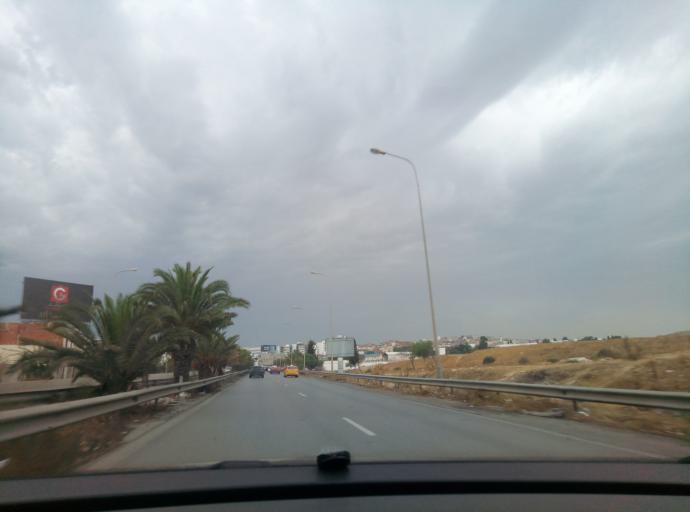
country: TN
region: Bin 'Arus
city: Ben Arous
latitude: 36.7714
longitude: 10.1973
